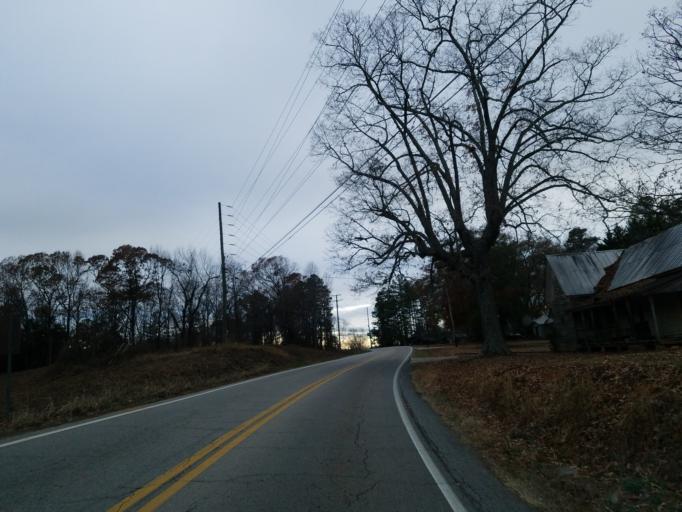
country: US
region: Georgia
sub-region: Dawson County
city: Dawsonville
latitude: 34.3859
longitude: -84.0114
